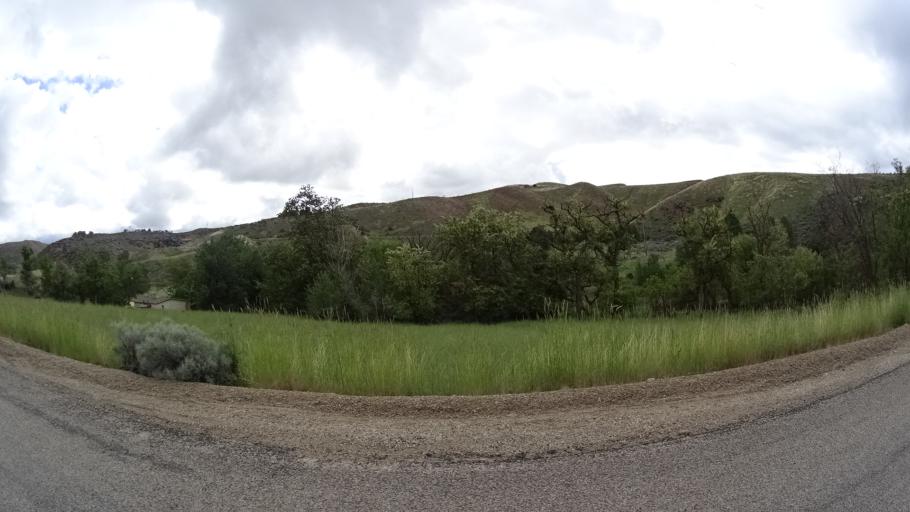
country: US
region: Idaho
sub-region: Ada County
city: Garden City
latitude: 43.6856
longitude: -116.2523
